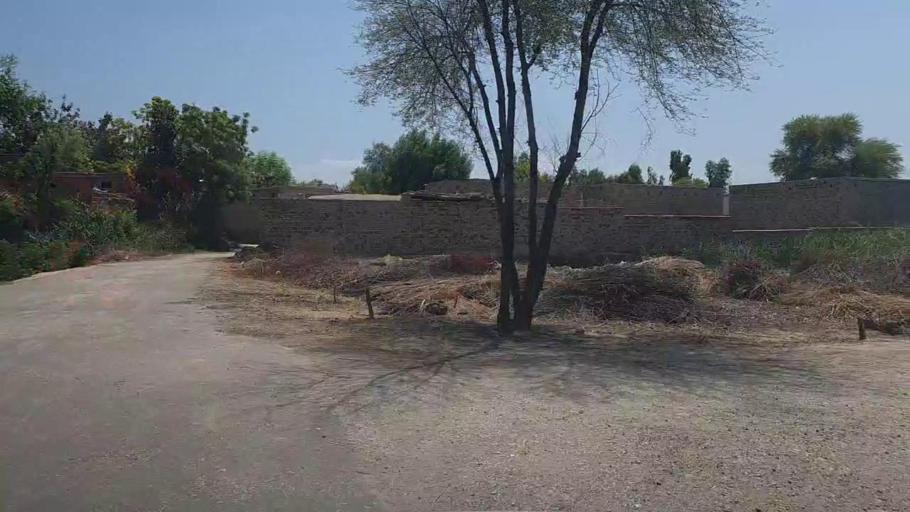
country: PK
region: Sindh
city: Ubauro
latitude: 28.1559
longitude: 69.7499
